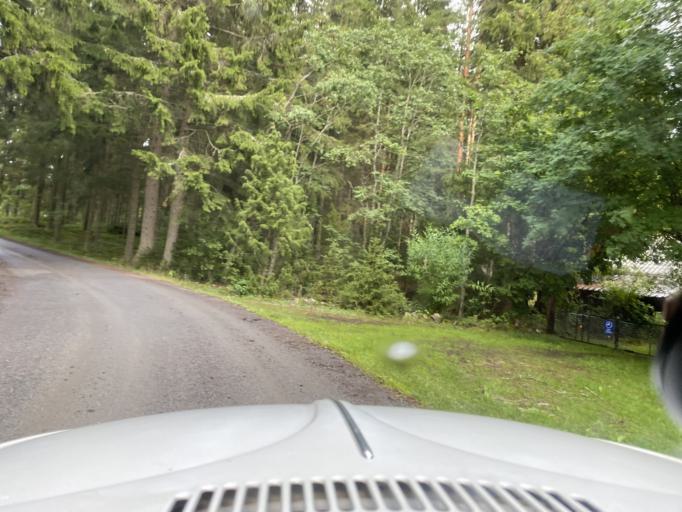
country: FI
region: Pirkanmaa
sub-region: Lounais-Pirkanmaa
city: Punkalaidun
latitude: 61.1298
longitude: 23.0660
